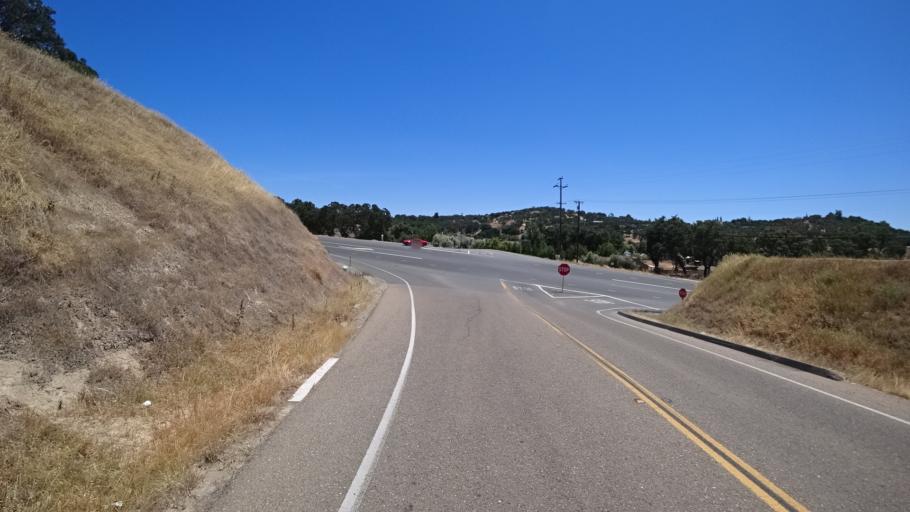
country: US
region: California
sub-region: Calaveras County
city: Rancho Calaveras
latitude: 38.1595
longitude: -120.8470
